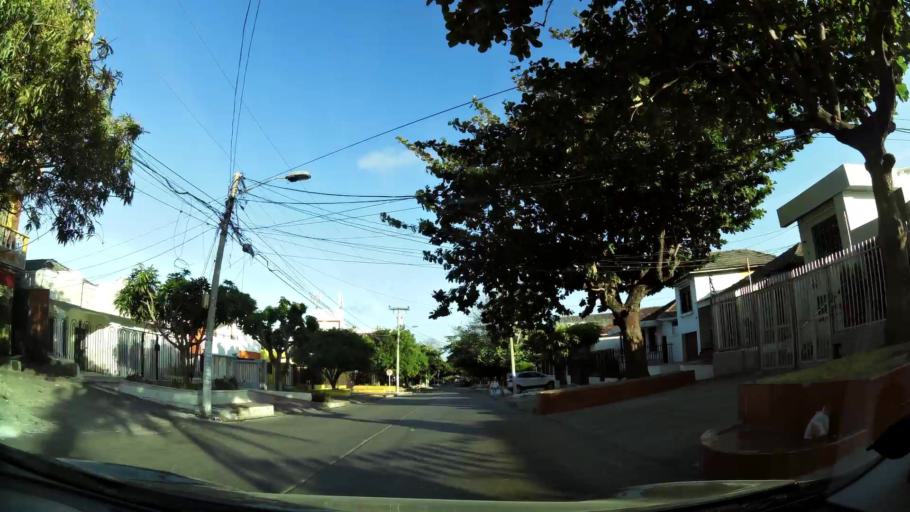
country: CO
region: Atlantico
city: Barranquilla
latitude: 10.9836
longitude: -74.7953
